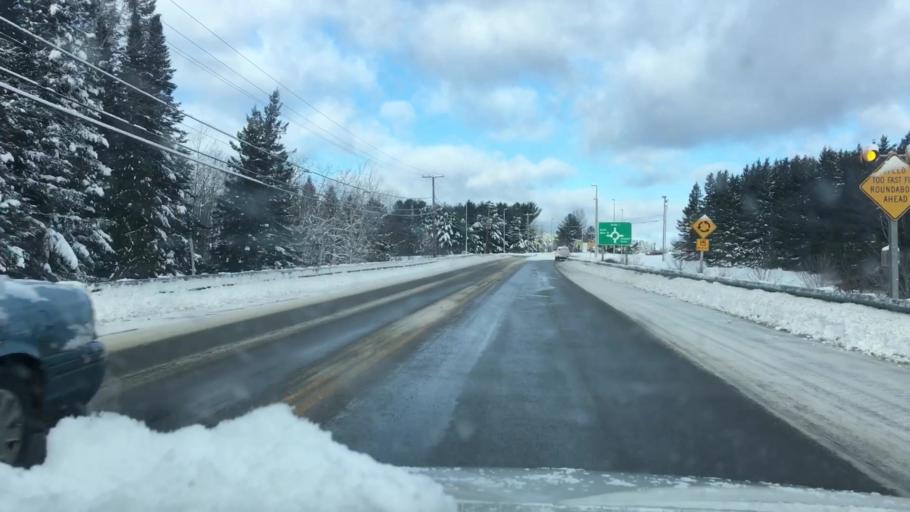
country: US
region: Maine
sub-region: Aroostook County
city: Caribou
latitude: 46.8773
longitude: -68.0085
